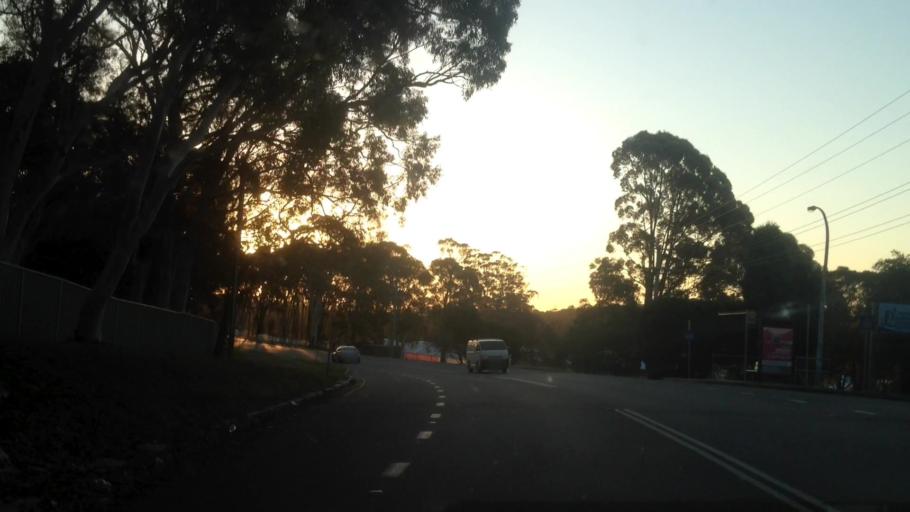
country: AU
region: New South Wales
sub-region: Wyong Shire
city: Kingfisher Shores
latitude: -33.1522
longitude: 151.5238
